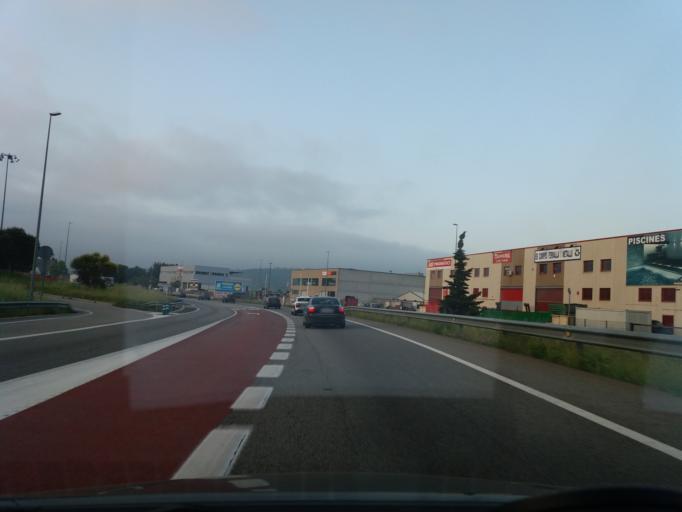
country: ES
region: Catalonia
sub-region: Provincia de Barcelona
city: Olesa de Montserrat
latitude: 41.5546
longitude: 1.8787
